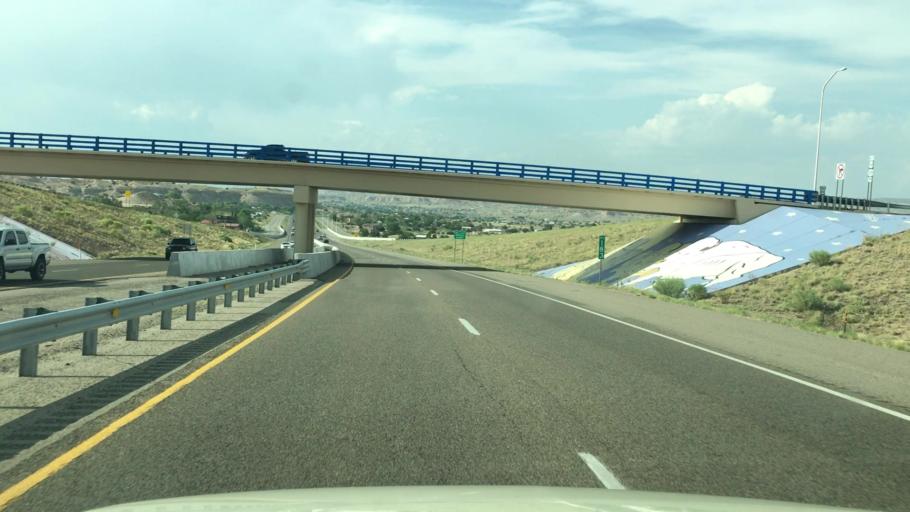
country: US
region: New Mexico
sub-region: Santa Fe County
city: Pojoaque
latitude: 35.9281
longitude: -106.0175
